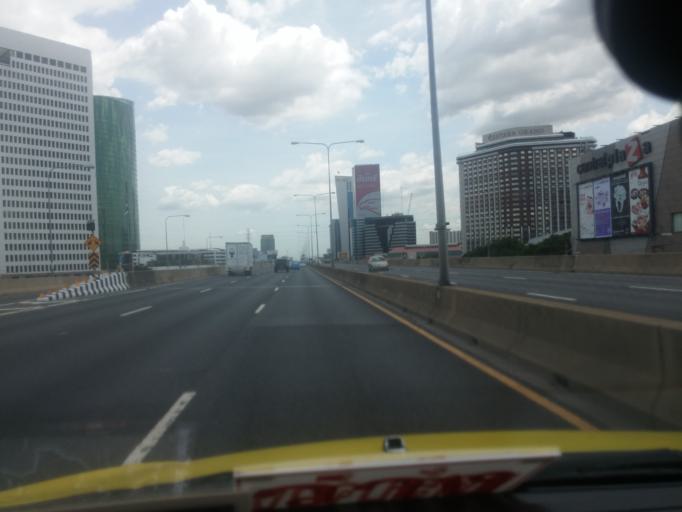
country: TH
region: Bangkok
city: Chatuchak
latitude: 13.8149
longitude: 100.5591
